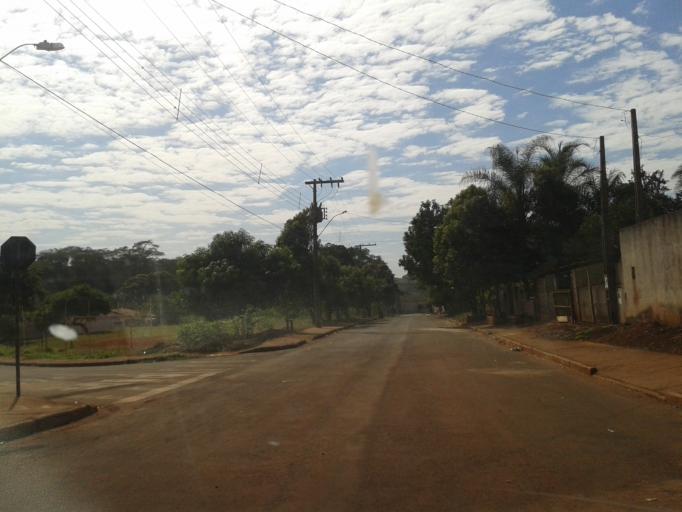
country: BR
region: Minas Gerais
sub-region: Ituiutaba
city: Ituiutaba
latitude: -18.9471
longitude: -49.4620
